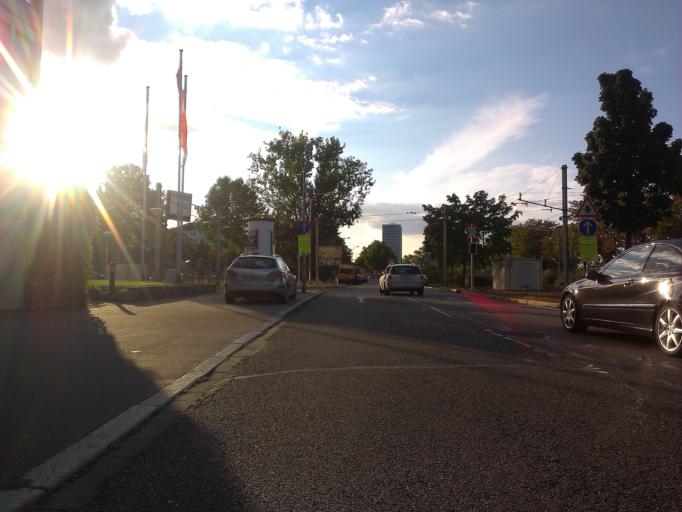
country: DE
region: Baden-Wuerttemberg
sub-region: Karlsruhe Region
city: Mannheim
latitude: 49.4917
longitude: 8.4761
